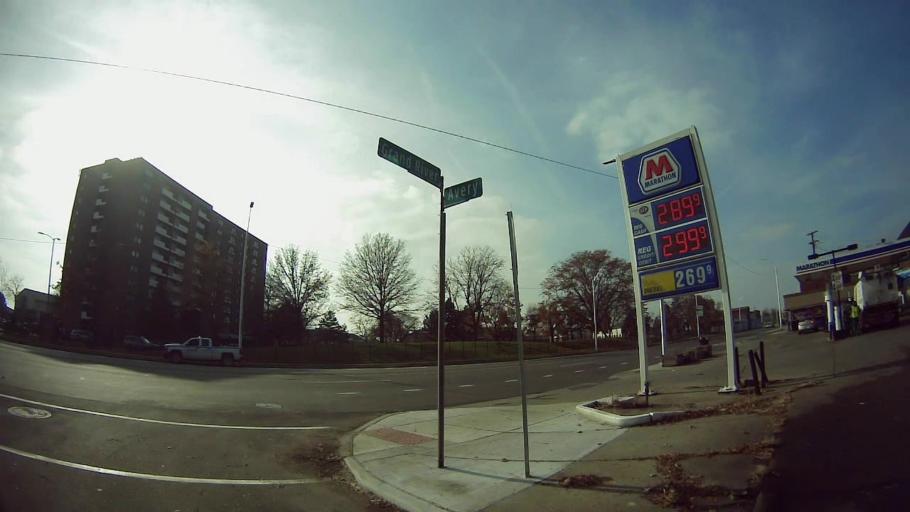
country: US
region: Michigan
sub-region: Wayne County
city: Detroit
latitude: 42.3441
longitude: -83.0771
